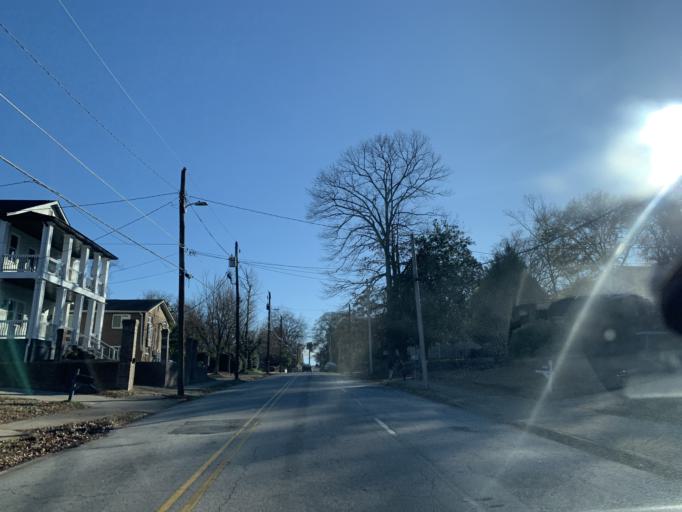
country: US
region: Georgia
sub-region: Fulton County
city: Atlanta
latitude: 33.7302
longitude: -84.3910
